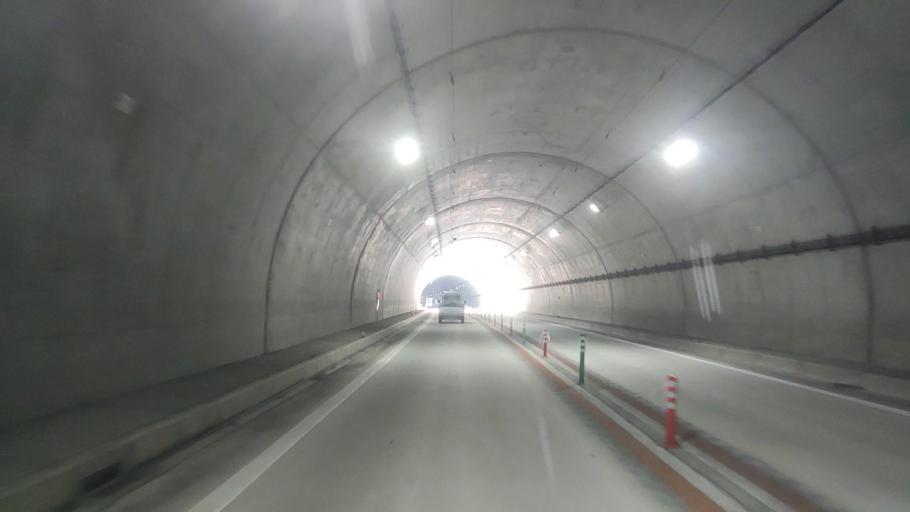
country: JP
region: Wakayama
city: Tanabe
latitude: 33.5831
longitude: 135.4511
